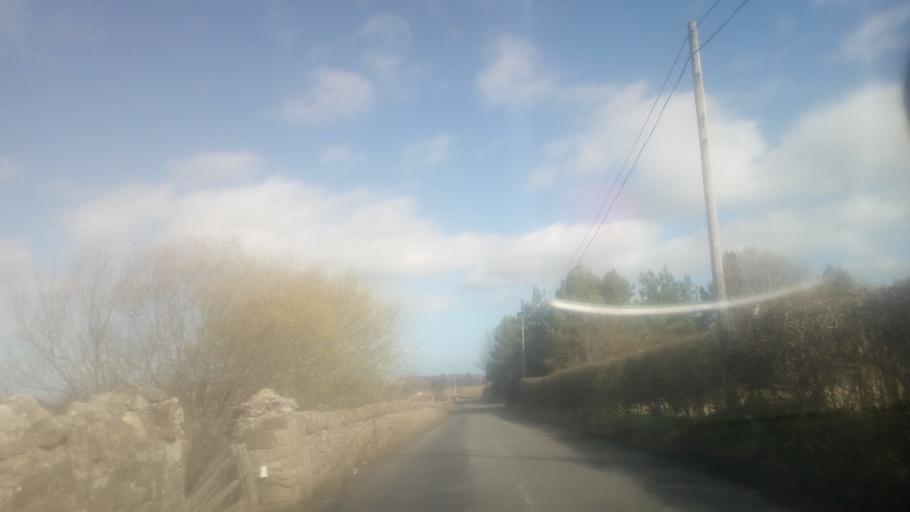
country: GB
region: Scotland
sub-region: Fife
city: Pathhead
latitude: 55.8696
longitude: -2.9683
